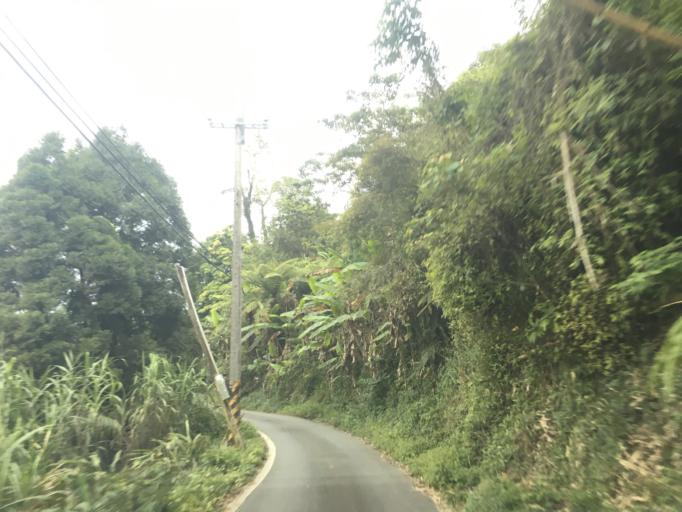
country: TW
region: Taiwan
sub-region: Nantou
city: Puli
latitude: 23.9678
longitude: 120.8366
